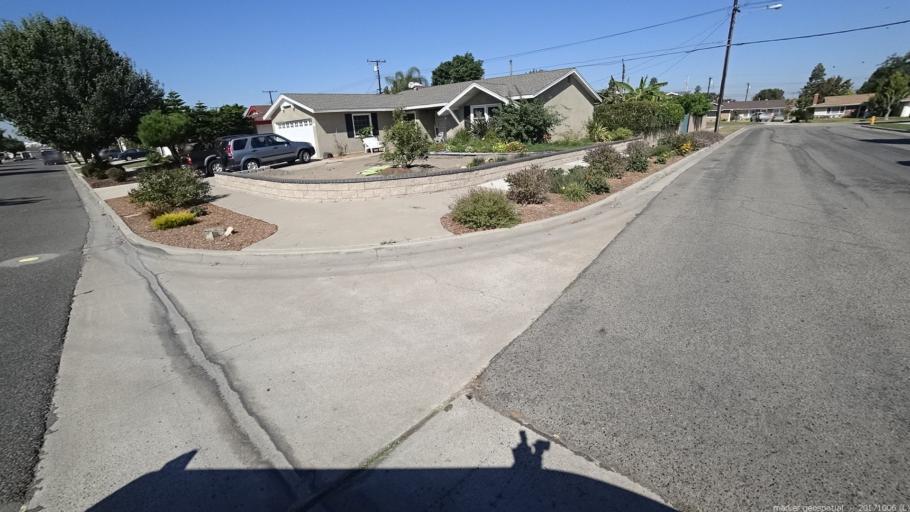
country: US
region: California
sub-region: Orange County
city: Westminster
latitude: 33.7869
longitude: -118.0234
